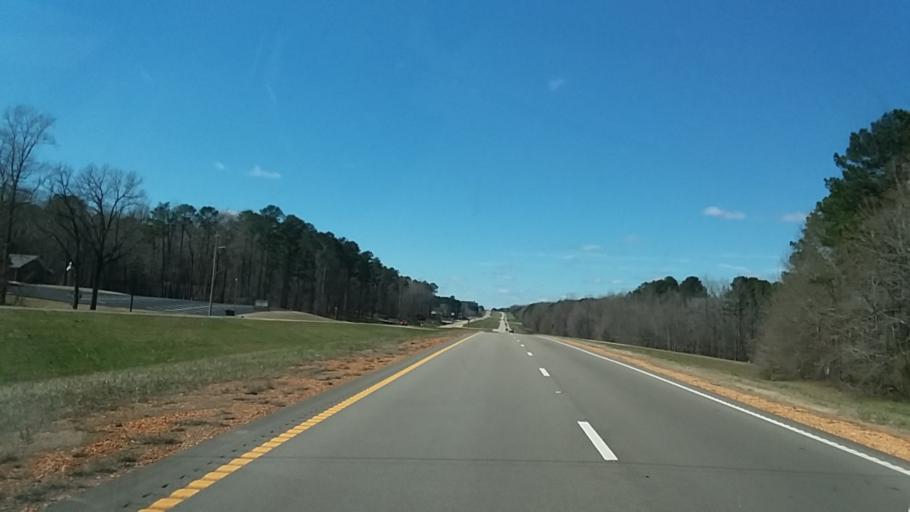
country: US
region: Mississippi
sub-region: Alcorn County
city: Farmington
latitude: 34.8671
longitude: -88.4204
